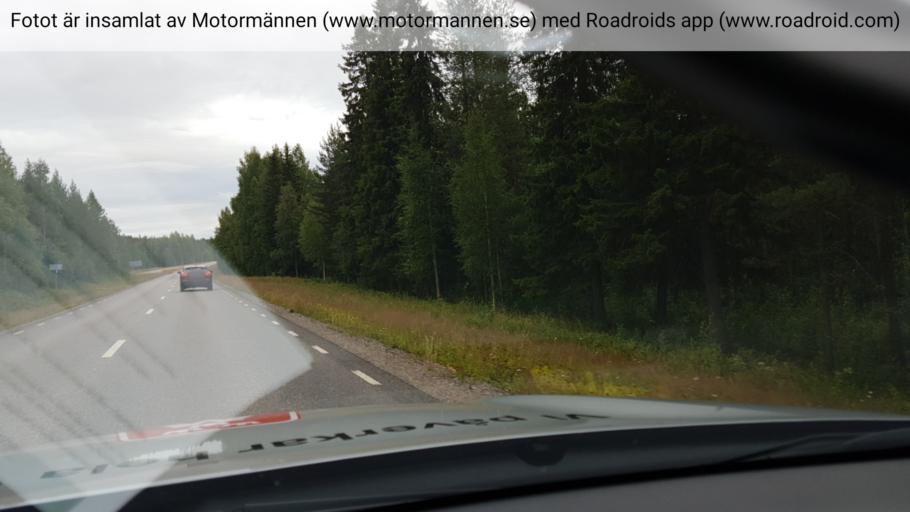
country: SE
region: Norrbotten
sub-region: Overkalix Kommun
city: OEverkalix
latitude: 66.5561
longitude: 22.7599
